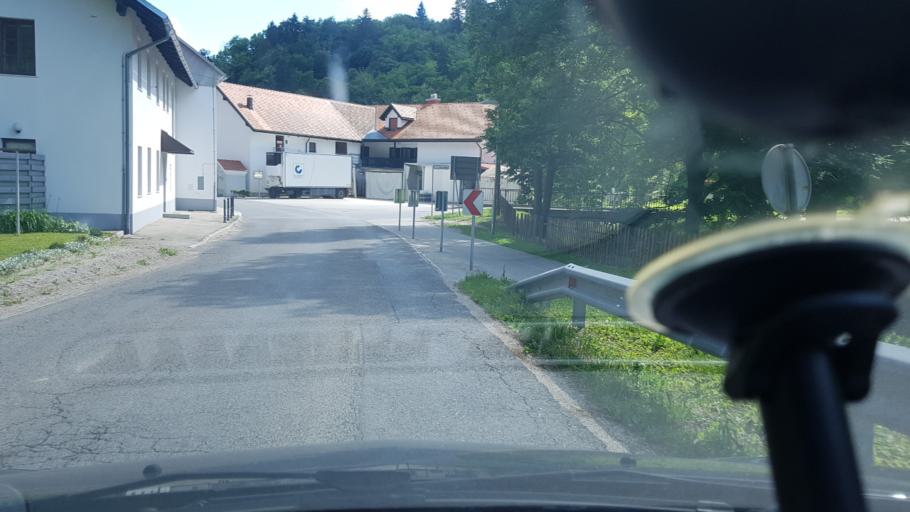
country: SI
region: Rogatec
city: Rogatec
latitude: 46.2302
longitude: 15.6985
